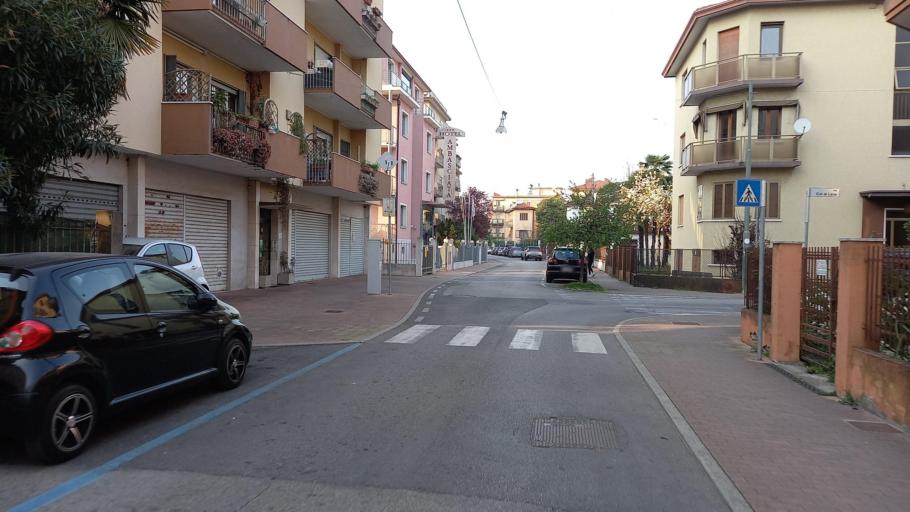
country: IT
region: Veneto
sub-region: Provincia di Venezia
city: Mestre
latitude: 45.4843
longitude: 12.2290
